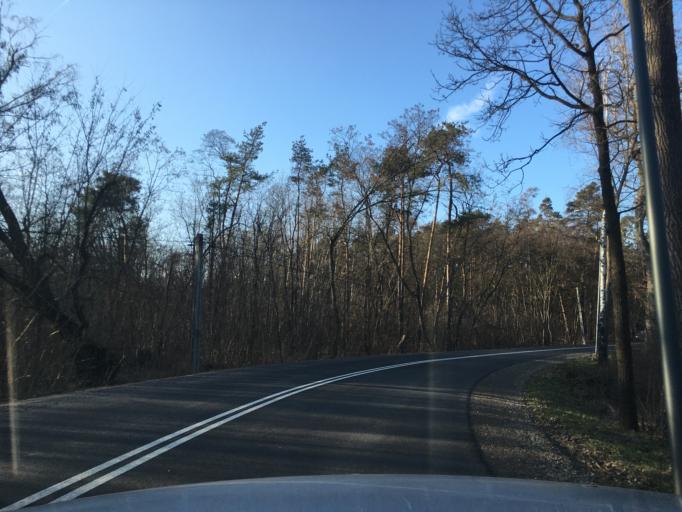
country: PL
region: Lodz Voivodeship
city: Zabia Wola
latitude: 52.0488
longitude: 20.7401
